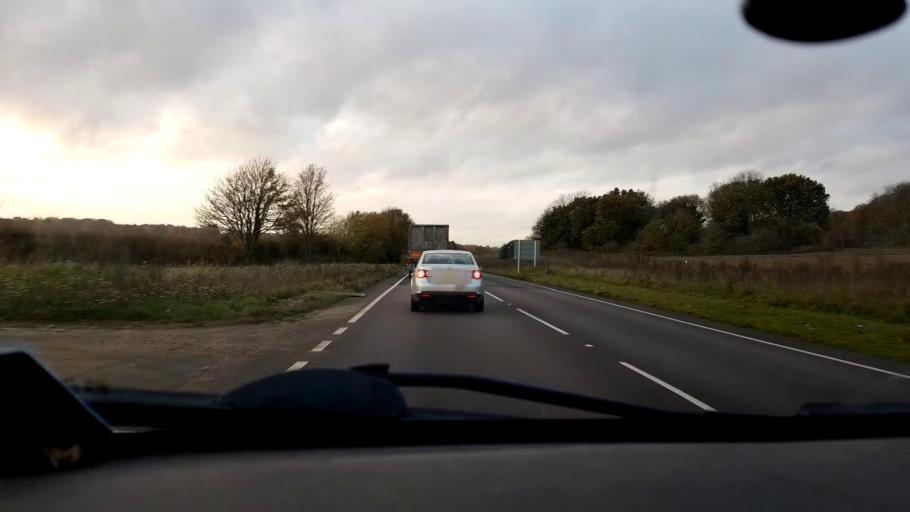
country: GB
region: England
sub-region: Norfolk
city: Costessey
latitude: 52.6954
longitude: 1.1703
